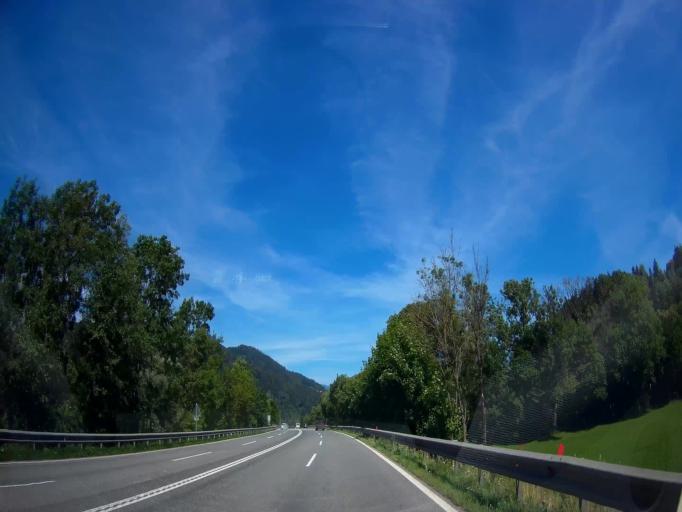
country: AT
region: Carinthia
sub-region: Politischer Bezirk Sankt Veit an der Glan
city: Micheldorf
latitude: 46.9154
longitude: 14.4362
